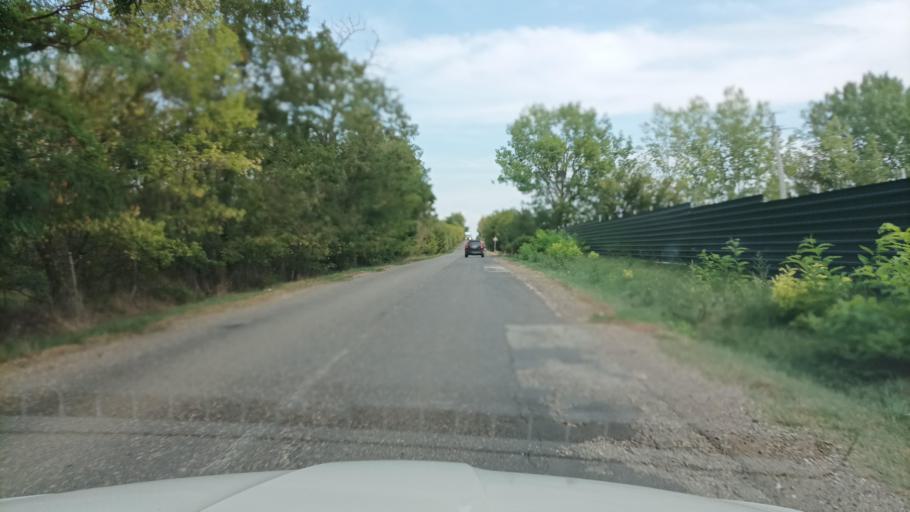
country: HU
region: Pest
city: Tura
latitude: 47.6206
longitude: 19.6143
